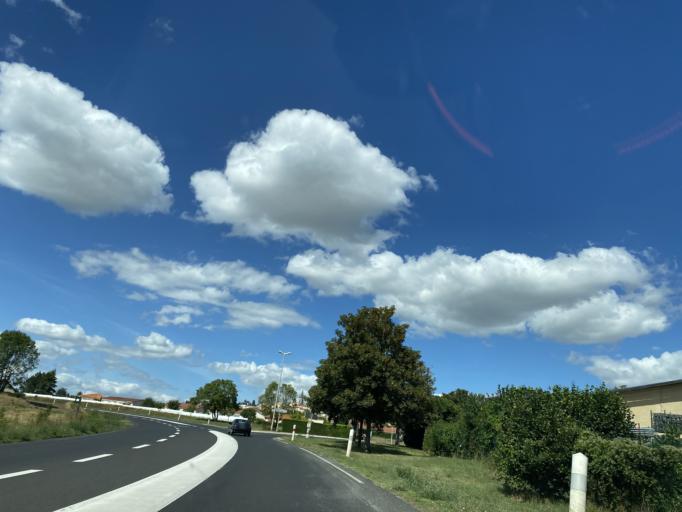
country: FR
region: Auvergne
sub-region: Departement du Puy-de-Dome
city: Mezel
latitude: 45.7484
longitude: 3.2397
